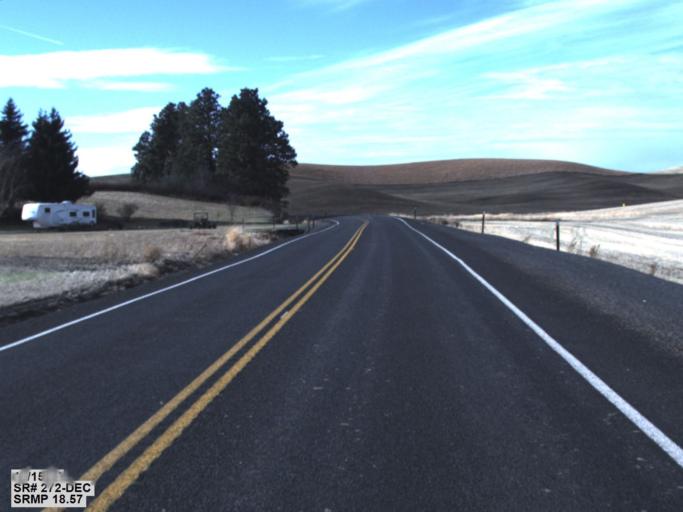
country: US
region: Idaho
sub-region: Latah County
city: Moscow
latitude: 46.9260
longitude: -117.0513
